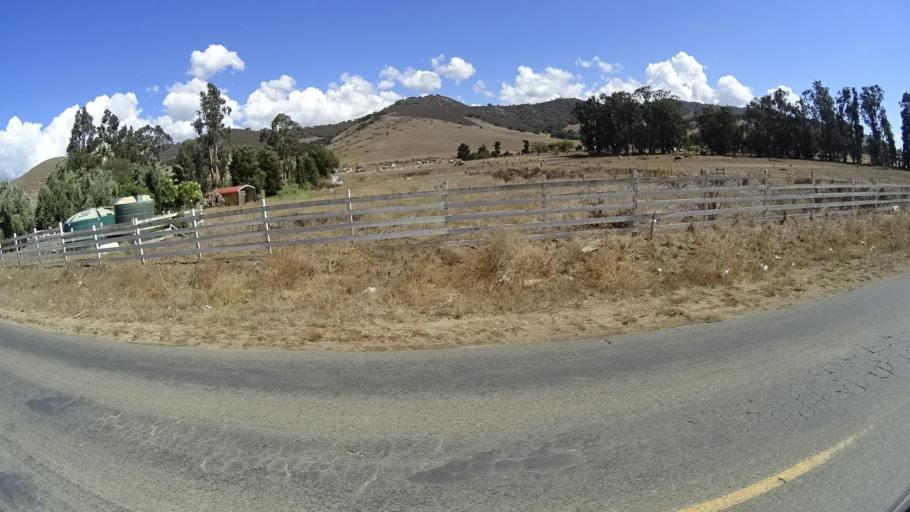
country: US
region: California
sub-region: Monterey County
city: Salinas
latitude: 36.6749
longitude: -121.5550
